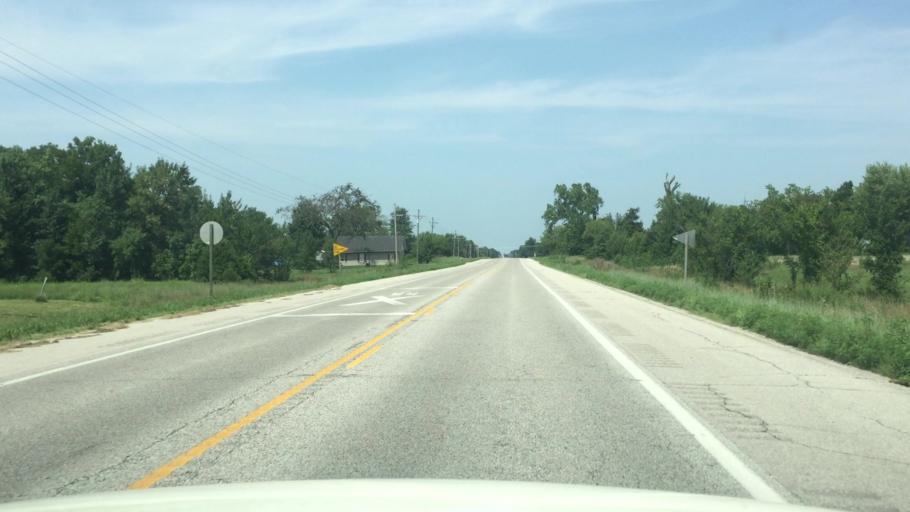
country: US
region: Kansas
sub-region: Cherokee County
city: Galena
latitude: 37.1157
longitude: -94.7043
